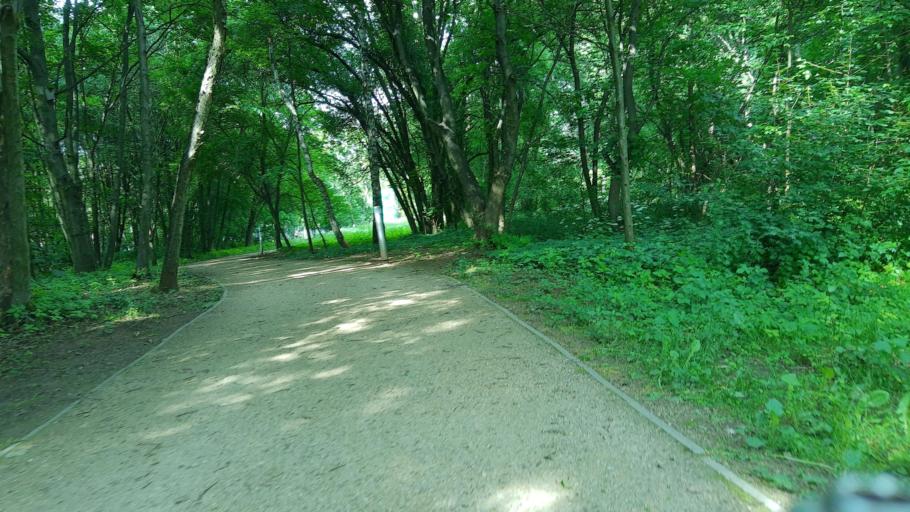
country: PL
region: Lodz Voivodeship
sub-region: Powiat sieradzki
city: Sieradz
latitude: 51.5948
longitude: 18.7545
